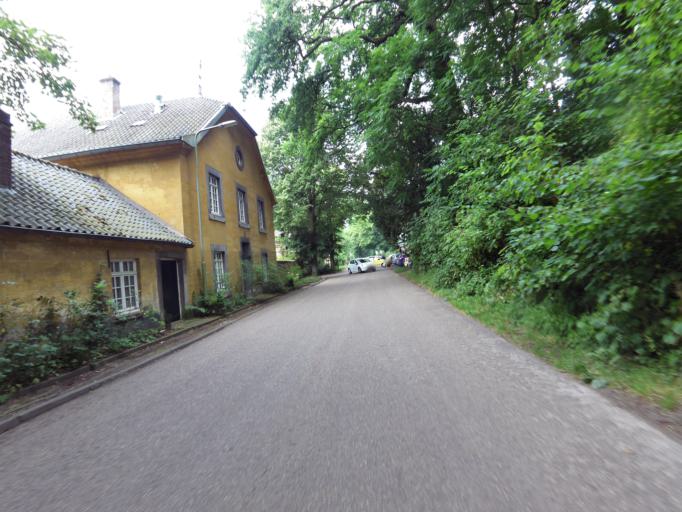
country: NL
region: Limburg
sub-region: Valkenburg aan de Geul
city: Valkenburg
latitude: 50.8621
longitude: 5.8429
